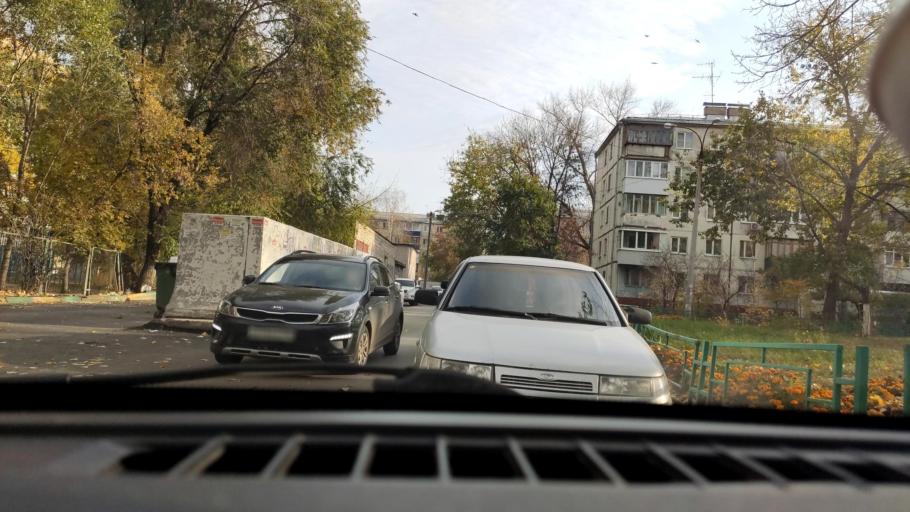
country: RU
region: Samara
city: Samara
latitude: 53.2108
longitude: 50.1910
